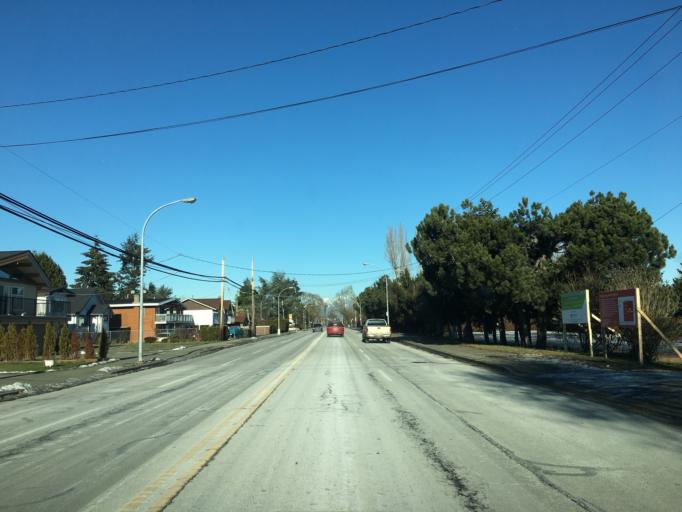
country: CA
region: British Columbia
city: Richmond
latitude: 49.1429
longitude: -123.0918
